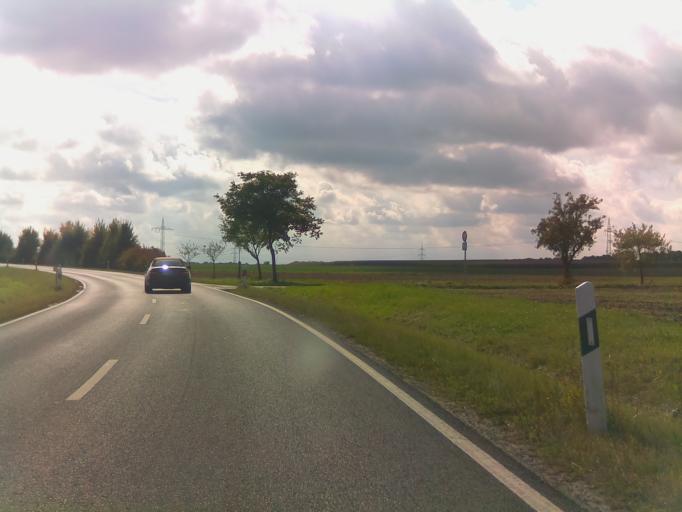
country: DE
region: Bavaria
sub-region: Regierungsbezirk Unterfranken
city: Biebelried
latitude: 49.7233
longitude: 10.0838
